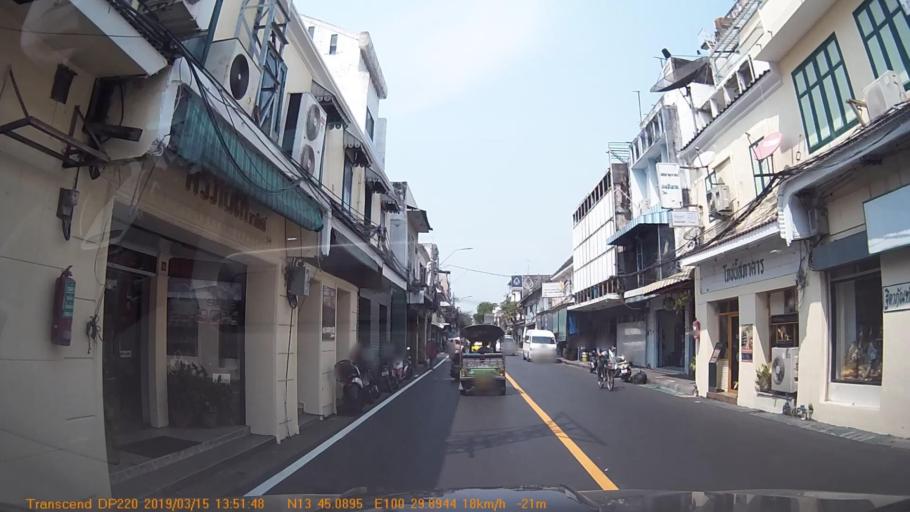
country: TH
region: Bangkok
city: Bangkok
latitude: 13.7516
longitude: 100.4983
